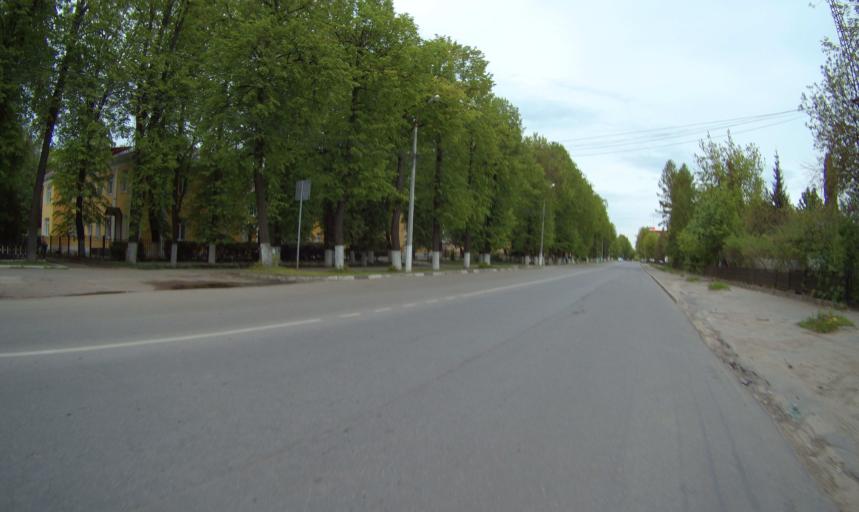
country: RU
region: Moskovskaya
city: Kolomna
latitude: 55.0734
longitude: 38.8019
